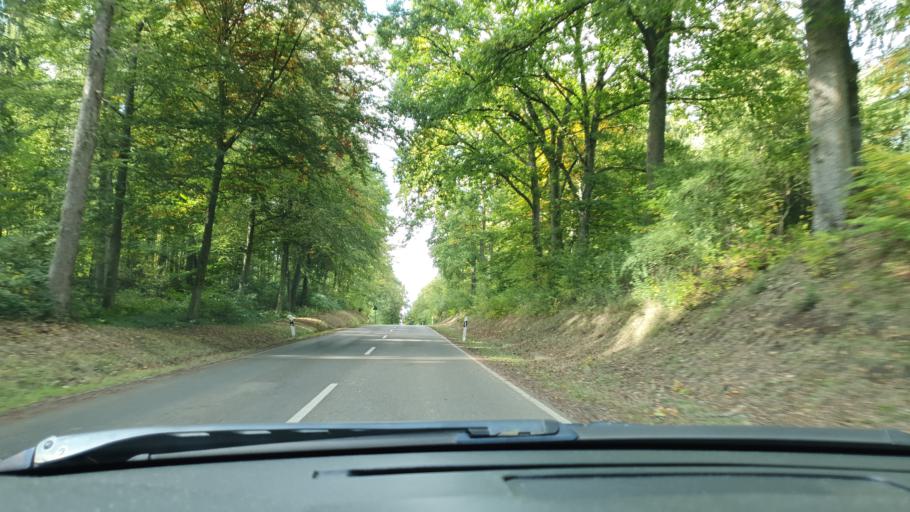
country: DE
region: Rheinland-Pfalz
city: Kaiserslautern
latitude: 49.4333
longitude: 7.8211
